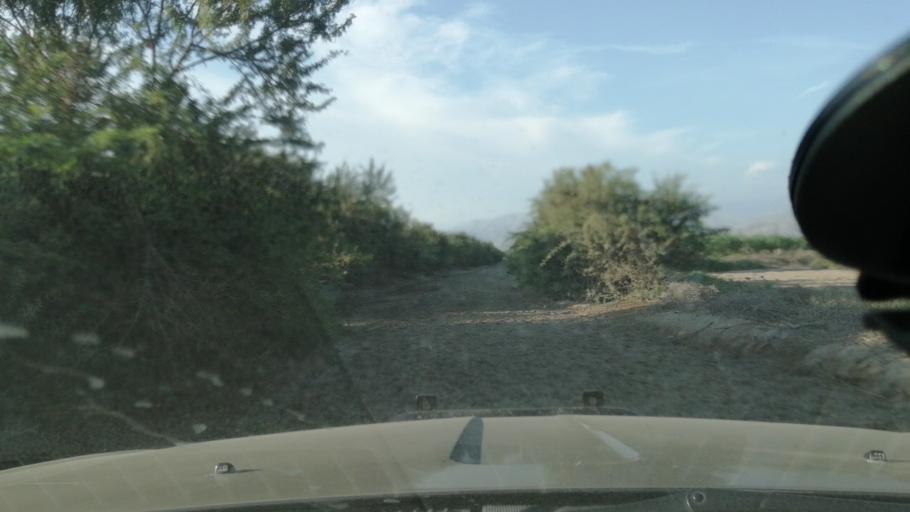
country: PE
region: Ica
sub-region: Provincia de Chincha
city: San Pedro
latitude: -13.3502
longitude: -76.1630
